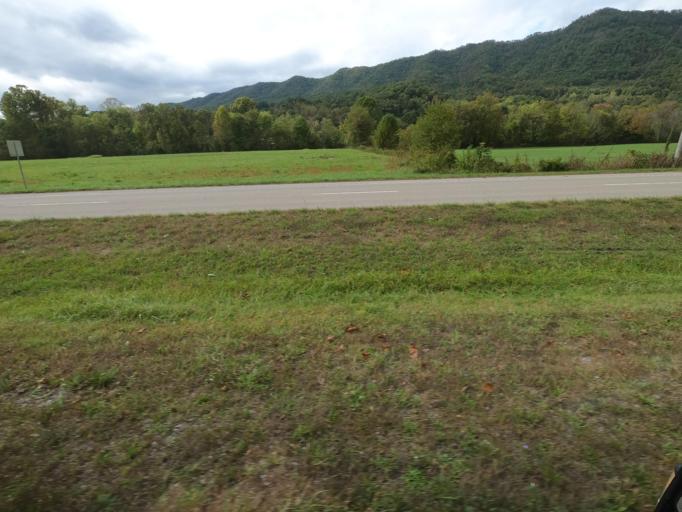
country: US
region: Tennessee
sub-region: Carter County
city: Elizabethton
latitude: 36.2725
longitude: -82.1791
